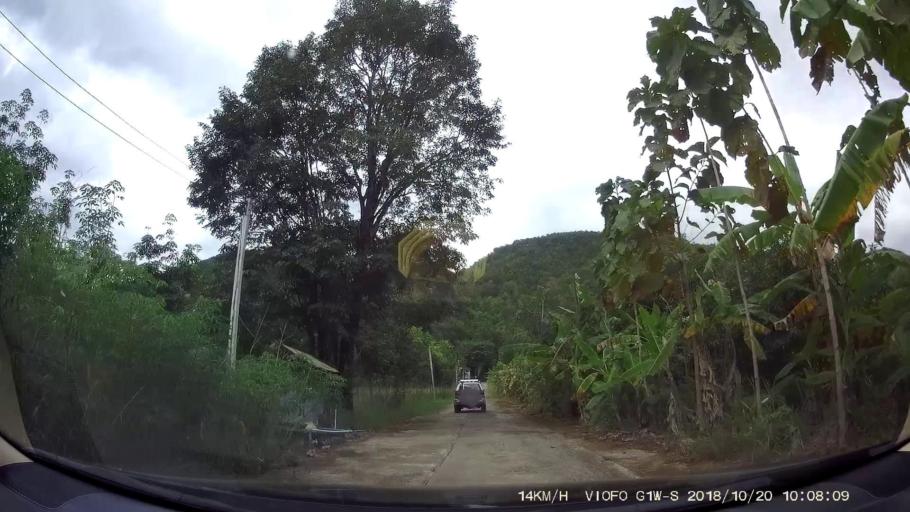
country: TH
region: Chaiyaphum
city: Khon San
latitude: 16.5501
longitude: 101.8520
